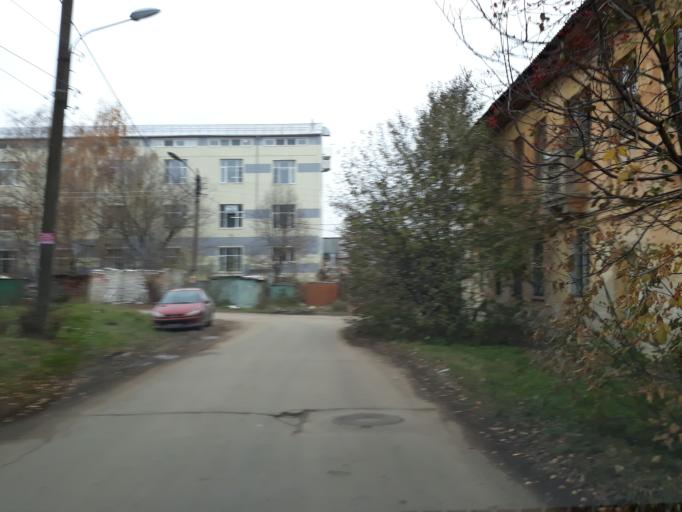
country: RU
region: Nizjnij Novgorod
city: Nizhniy Novgorod
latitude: 56.2473
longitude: 43.9751
